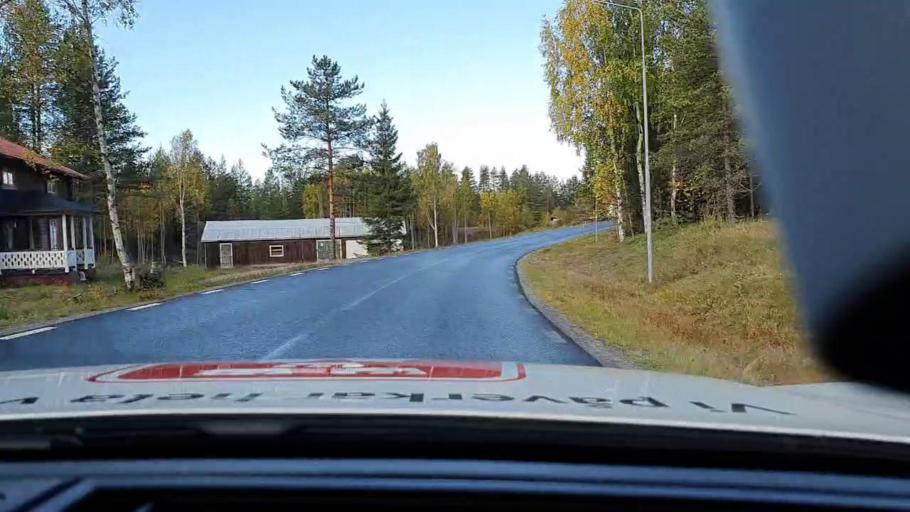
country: SE
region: Vaesterbotten
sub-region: Skelleftea Kommun
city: Langsele
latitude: 64.9469
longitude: 20.0228
